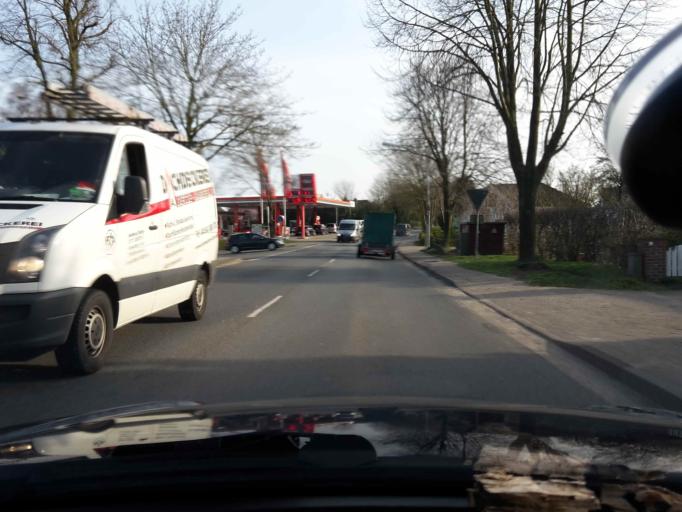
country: DE
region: Lower Saxony
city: Hollenstedt
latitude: 53.3661
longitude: 9.7115
